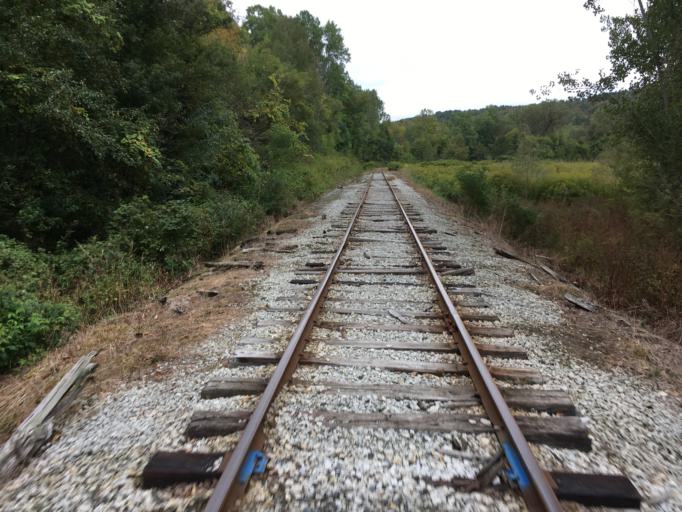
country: US
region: Vermont
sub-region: Washington County
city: Montpelier
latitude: 44.2315
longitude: -72.5498
